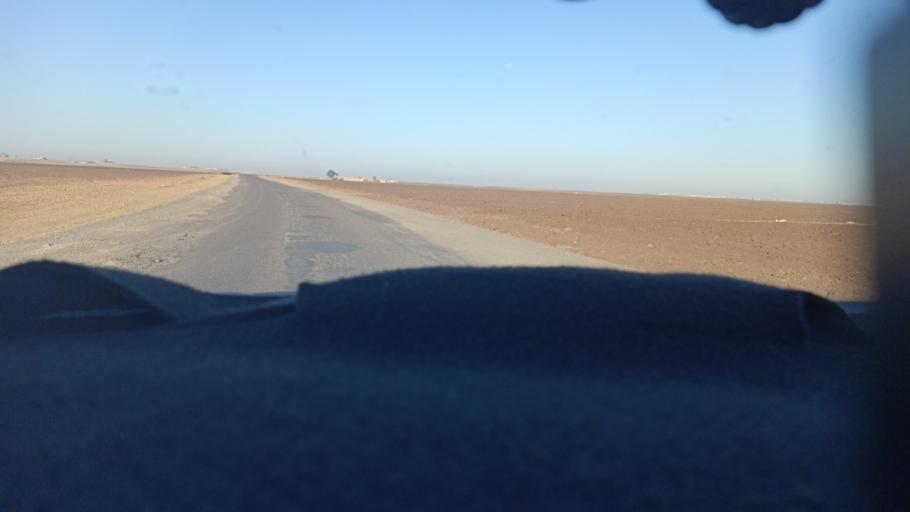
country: MA
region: Doukkala-Abda
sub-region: Safi
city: Youssoufia
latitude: 32.3721
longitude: -8.7064
